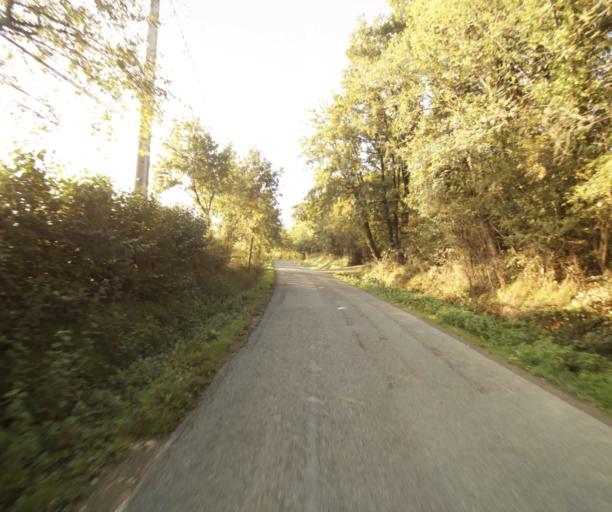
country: FR
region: Midi-Pyrenees
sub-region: Departement du Tarn-et-Garonne
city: Saint-Nauphary
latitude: 43.9403
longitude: 1.4414
